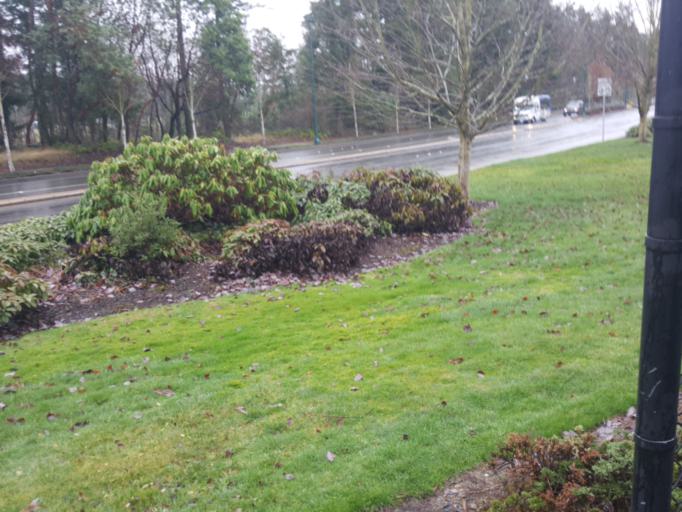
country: US
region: Washington
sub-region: Pierce County
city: University Place
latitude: 47.2128
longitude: -122.5372
